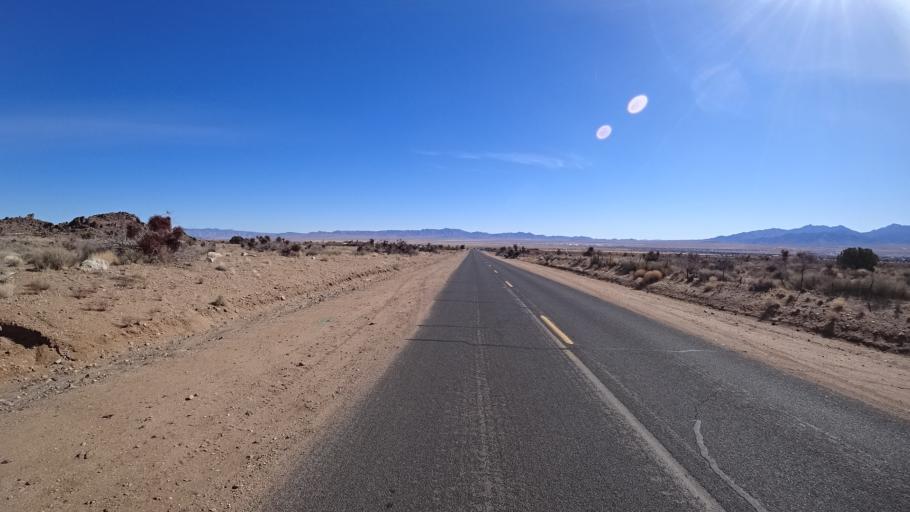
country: US
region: Arizona
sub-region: Mohave County
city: New Kingman-Butler
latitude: 35.2877
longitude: -114.0560
